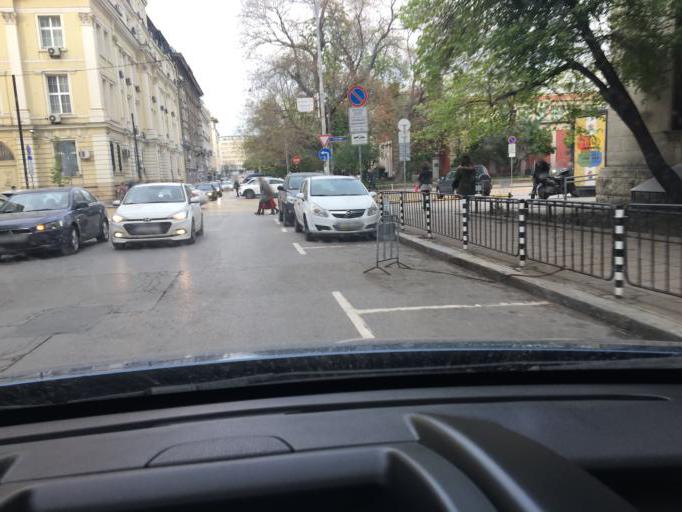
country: BG
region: Sofia-Capital
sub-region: Stolichna Obshtina
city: Sofia
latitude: 42.6940
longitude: 23.3232
